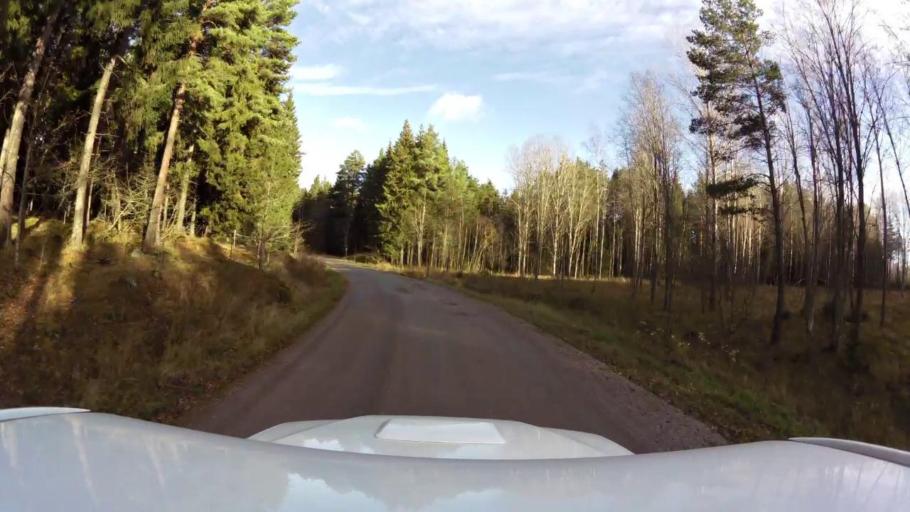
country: SE
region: OEstergoetland
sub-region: Linkopings Kommun
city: Linkoping
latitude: 58.3632
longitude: 15.6048
